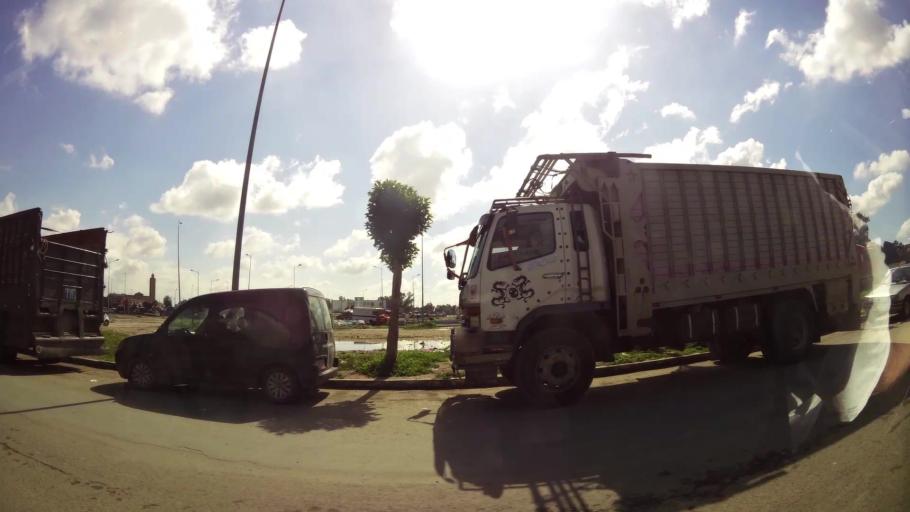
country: MA
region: Grand Casablanca
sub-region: Mediouna
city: Mediouna
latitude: 33.4551
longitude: -7.5160
